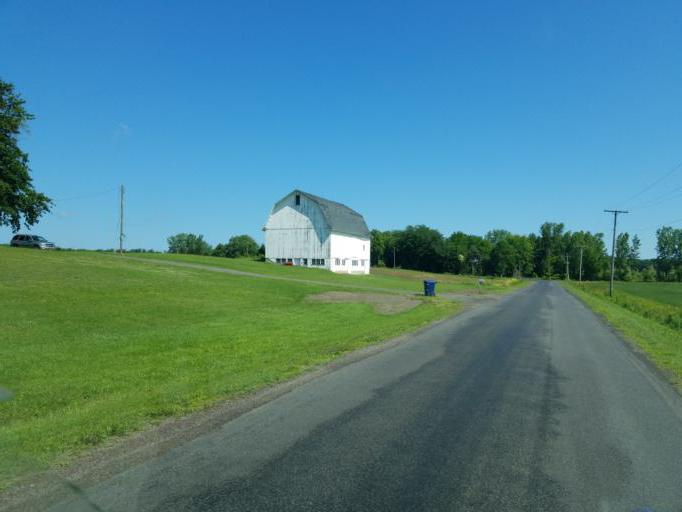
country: US
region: New York
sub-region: Wayne County
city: Wolcott
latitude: 43.1731
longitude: -76.8650
